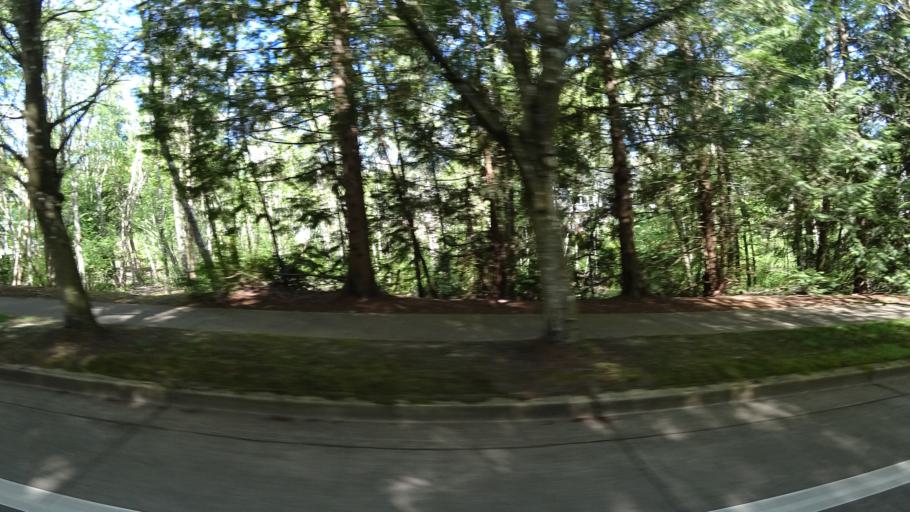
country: US
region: Oregon
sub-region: Washington County
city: King City
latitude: 45.4419
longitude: -122.8371
